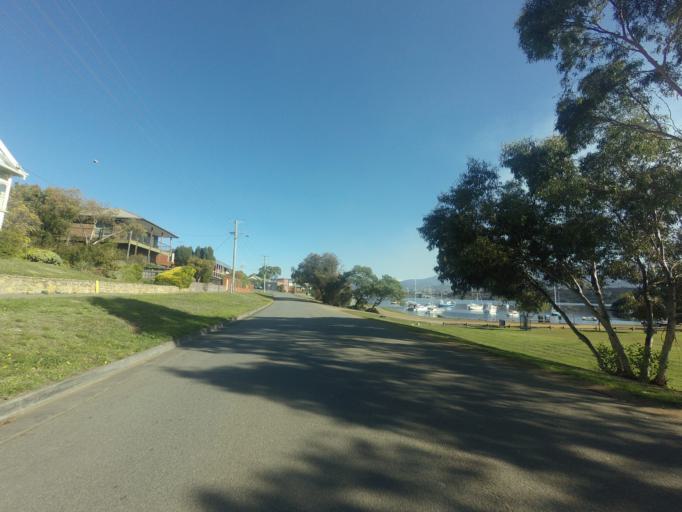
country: AU
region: Tasmania
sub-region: Clarence
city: Bellerive
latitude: -42.8652
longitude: 147.3559
